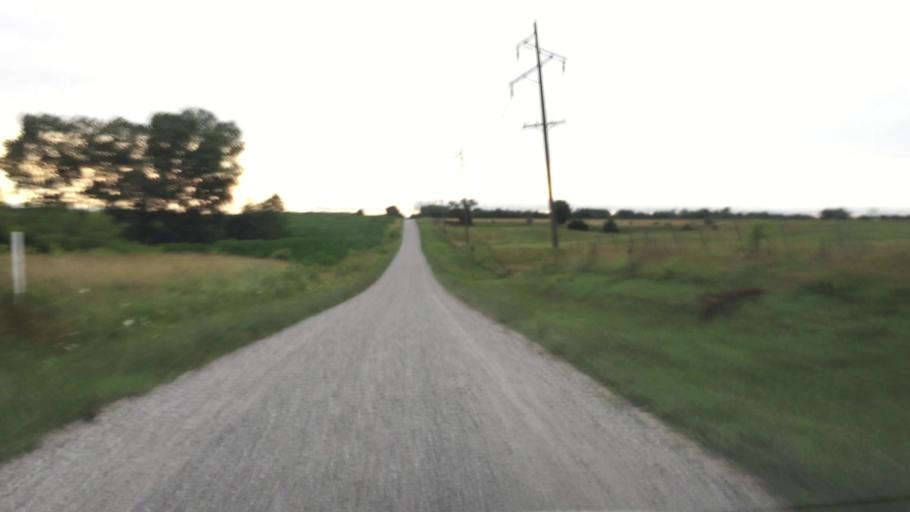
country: US
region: Illinois
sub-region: Hancock County
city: Hamilton
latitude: 40.4260
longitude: -91.3390
